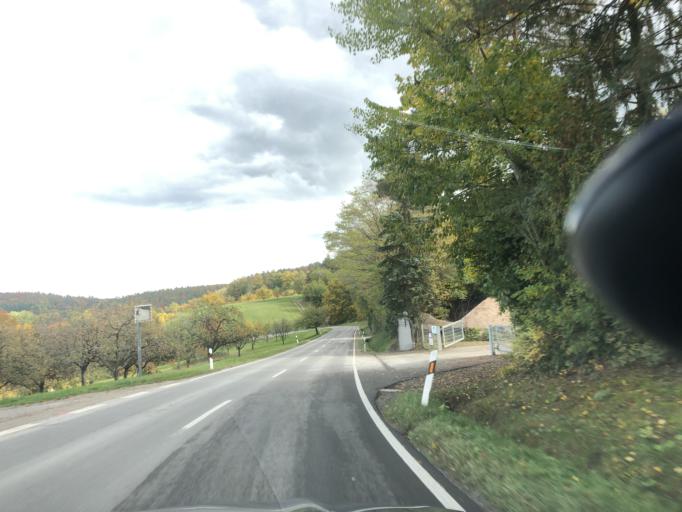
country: DE
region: Baden-Wuerttemberg
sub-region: Regierungsbezirk Stuttgart
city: Winterbach
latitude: 48.8250
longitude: 9.4641
